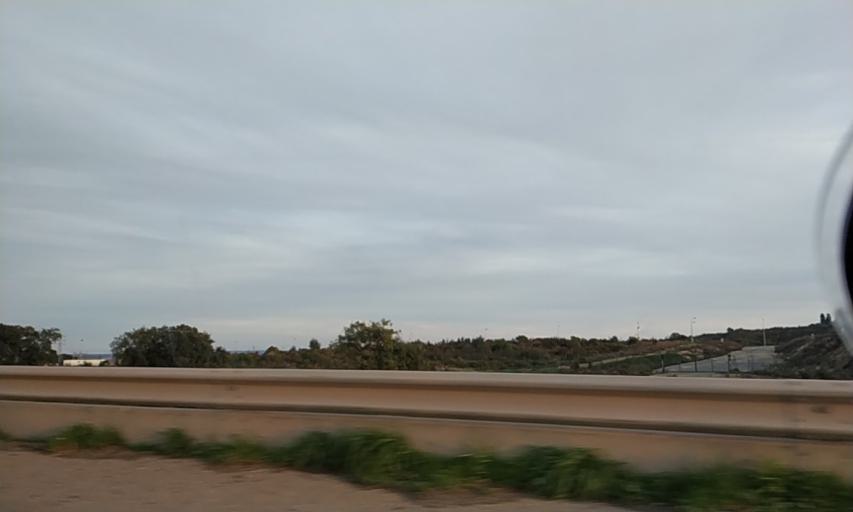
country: PT
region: Setubal
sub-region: Setubal
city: Setubal
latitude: 38.5082
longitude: -8.8387
